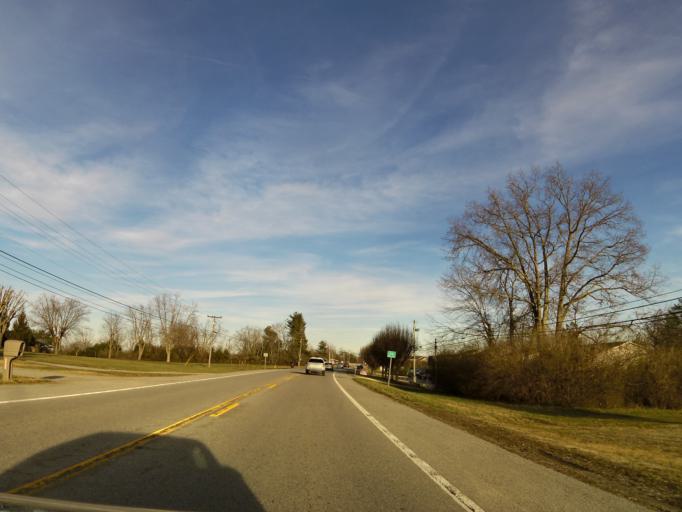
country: US
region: Tennessee
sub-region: Cumberland County
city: Crossville
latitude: 35.9579
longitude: -85.0727
